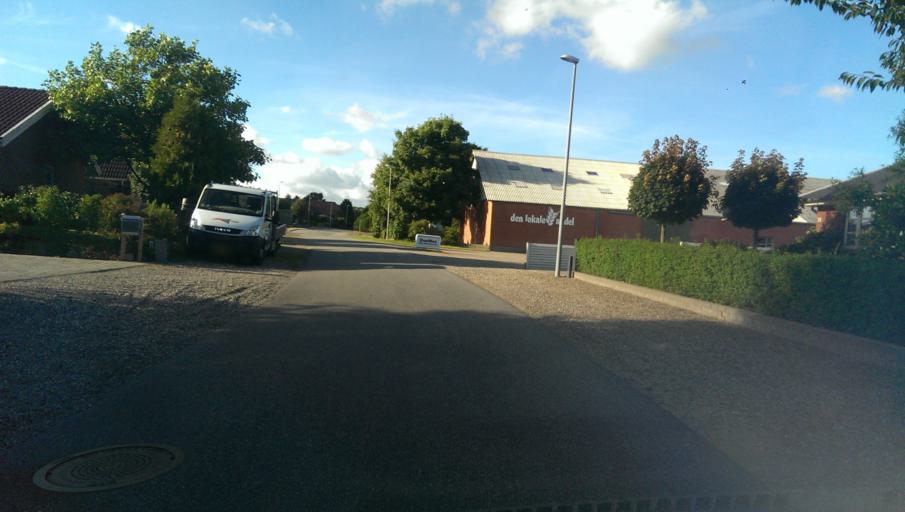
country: DK
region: South Denmark
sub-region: Esbjerg Kommune
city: Tjaereborg
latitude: 55.5059
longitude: 8.5581
